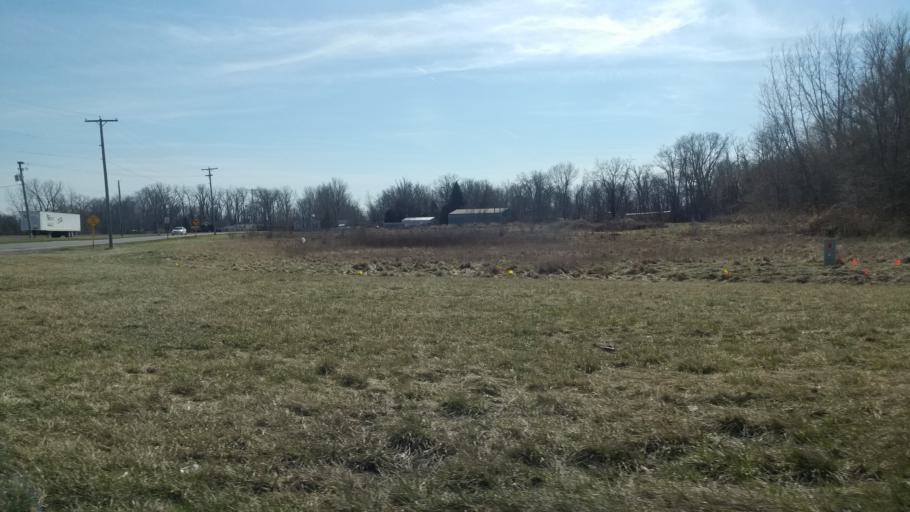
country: US
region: Ohio
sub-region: Hancock County
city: Findlay
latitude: 41.0588
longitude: -83.6776
